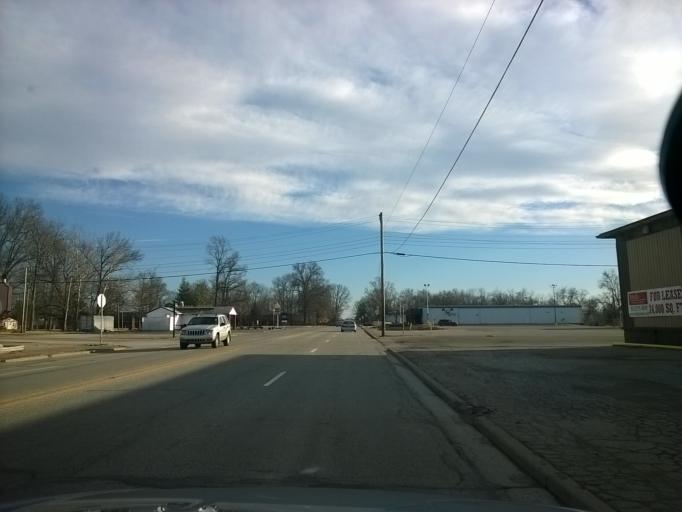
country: US
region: Indiana
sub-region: Scott County
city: Austin
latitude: 38.7471
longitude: -85.8075
